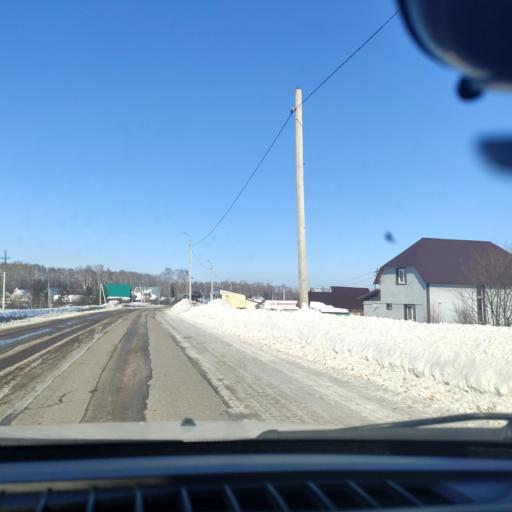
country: RU
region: Bashkortostan
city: Iglino
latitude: 54.8118
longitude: 56.3825
